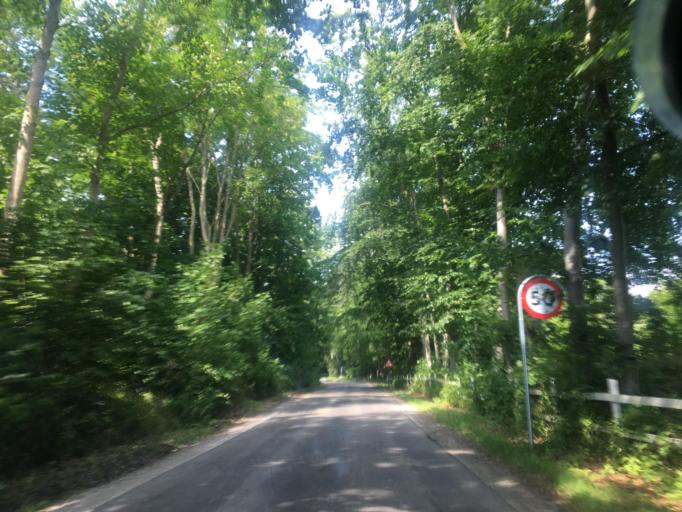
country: DK
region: Zealand
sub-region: Vordingborg Kommune
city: Praesto
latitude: 55.1829
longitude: 12.0812
